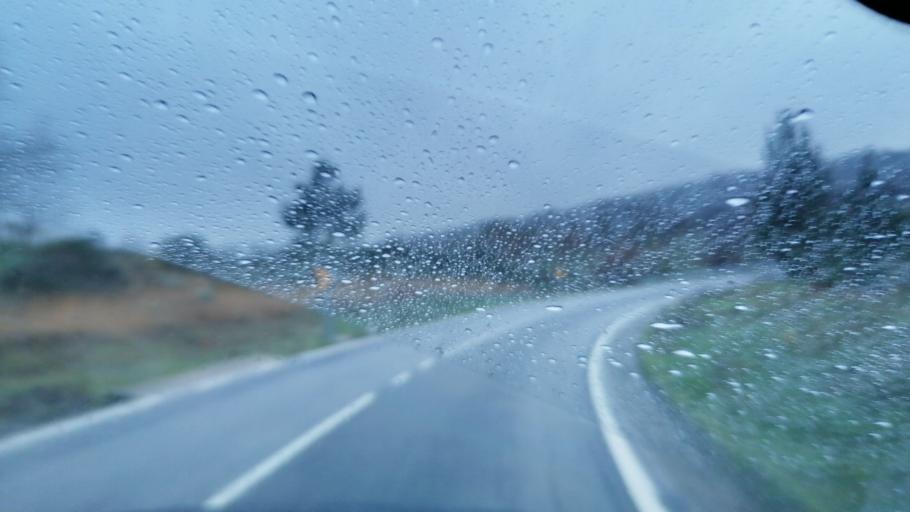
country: PT
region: Vila Real
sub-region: Murca
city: Murca
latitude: 41.4324
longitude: -7.5401
